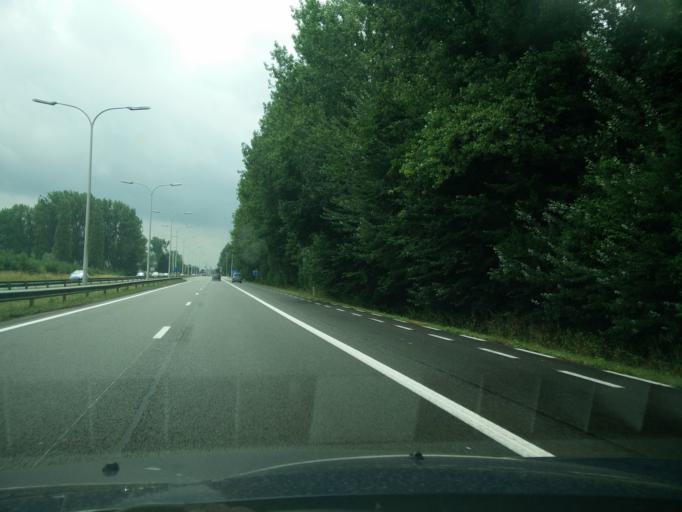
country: BE
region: Flanders
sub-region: Provincie Oost-Vlaanderen
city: Gavere
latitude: 50.9598
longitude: 3.6483
